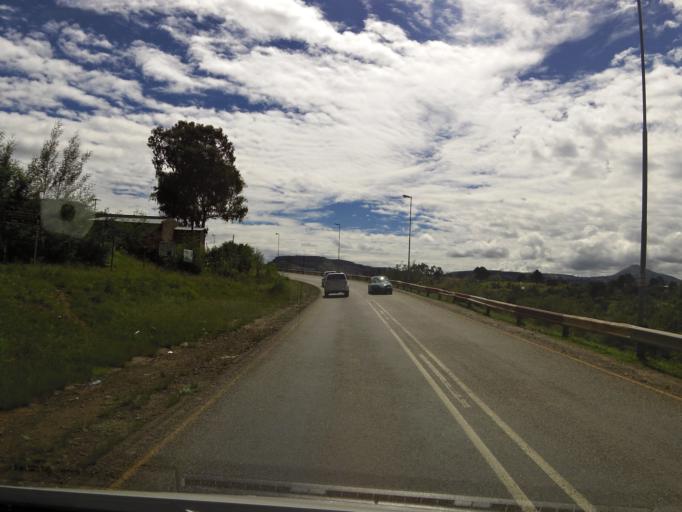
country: LS
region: Leribe
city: Leribe
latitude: -28.8792
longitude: 28.0473
